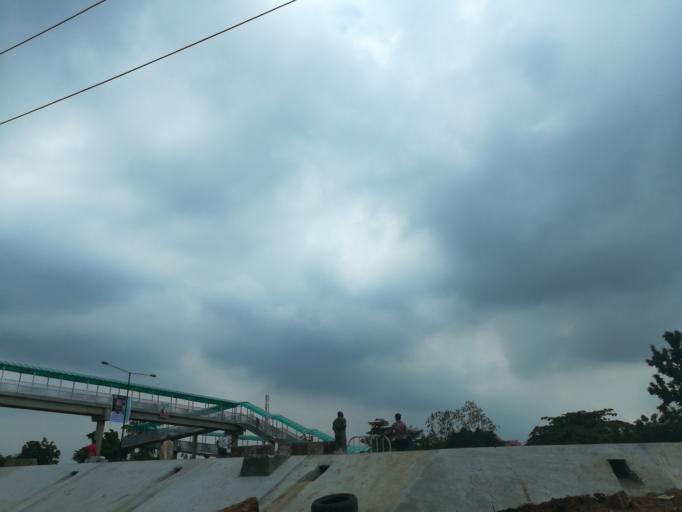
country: NG
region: Lagos
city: Ikeja
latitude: 6.6168
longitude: 3.3653
